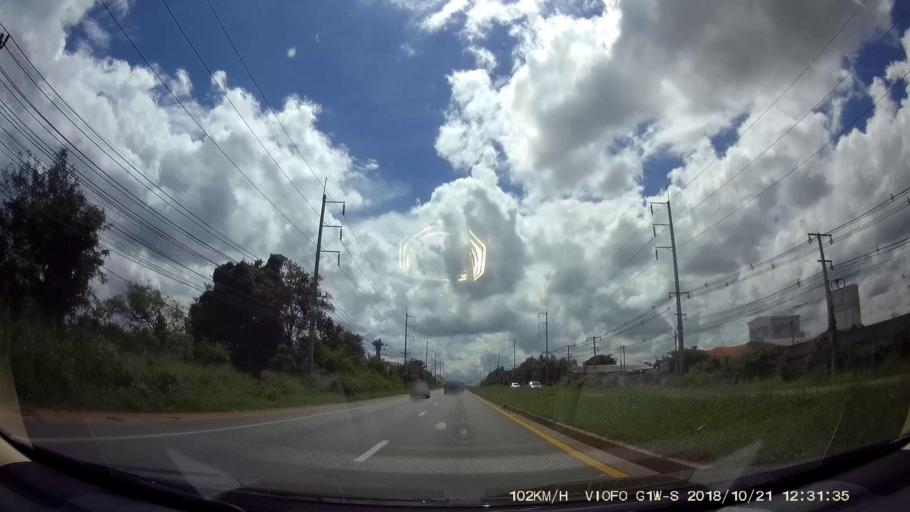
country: TH
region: Nakhon Ratchasima
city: Dan Khun Thot
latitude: 15.1545
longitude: 101.7343
